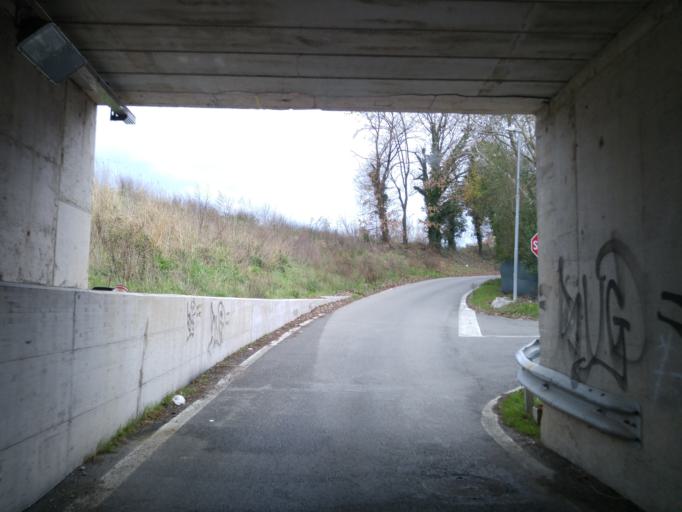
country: IT
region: The Marches
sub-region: Provincia di Pesaro e Urbino
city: Centinarola
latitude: 43.8325
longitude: 12.9945
